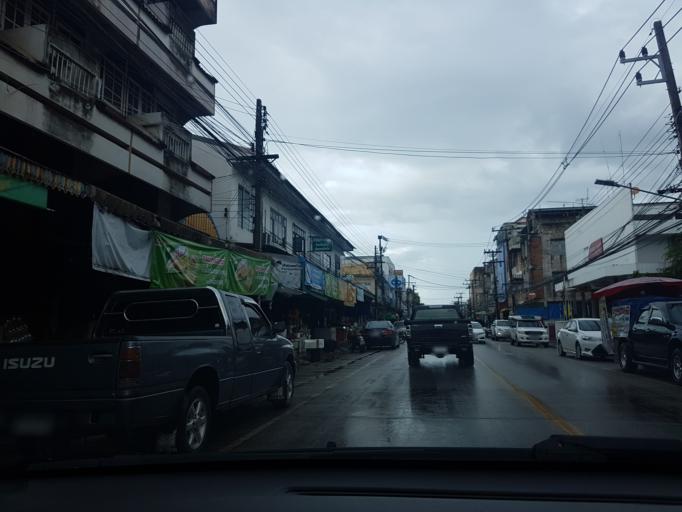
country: TH
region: Lampang
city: Lampang
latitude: 18.2810
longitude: 99.4736
